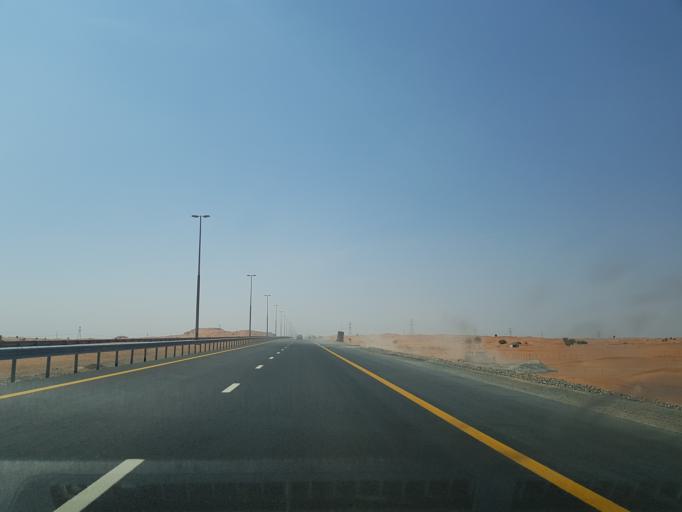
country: AE
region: Ash Shariqah
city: Adh Dhayd
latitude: 25.2437
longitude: 55.8642
